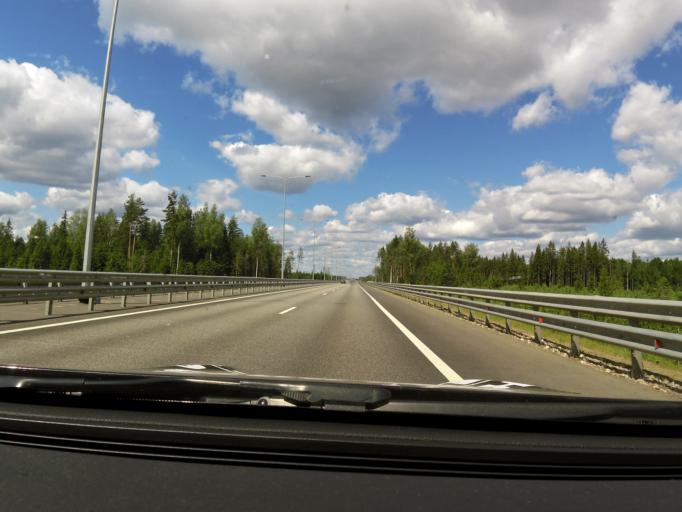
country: RU
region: Tverskaya
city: Krasnomayskiy
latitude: 57.4607
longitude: 34.3843
